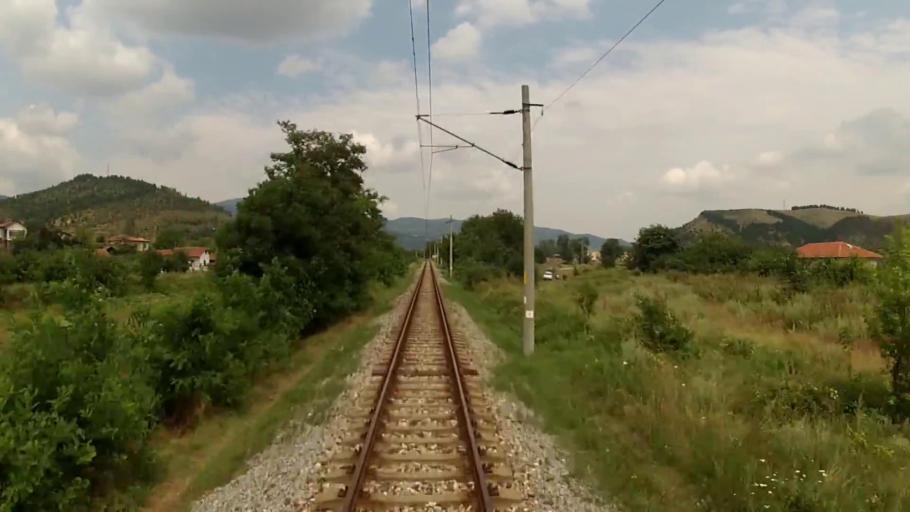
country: BG
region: Blagoevgrad
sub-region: Obshtina Simitli
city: Simitli
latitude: 41.8619
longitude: 23.1277
